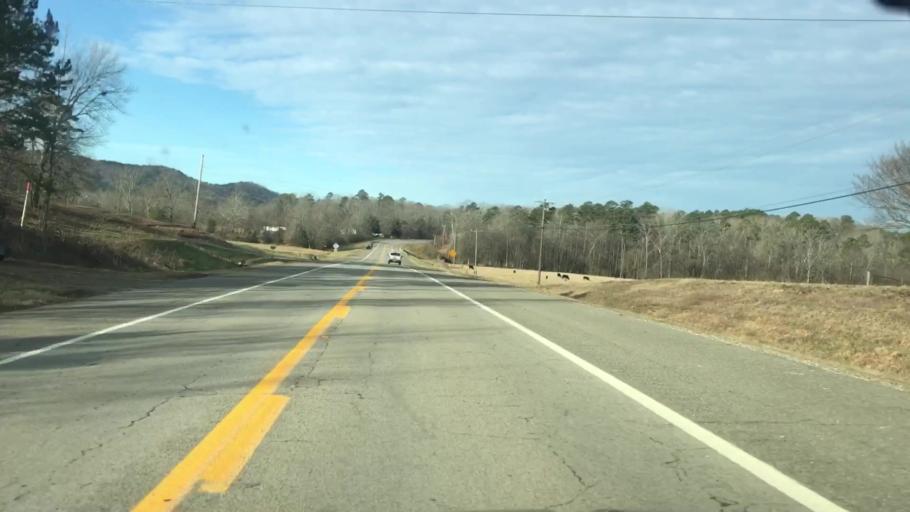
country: US
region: Arkansas
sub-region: Montgomery County
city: Mount Ida
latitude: 34.5400
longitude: -93.5972
